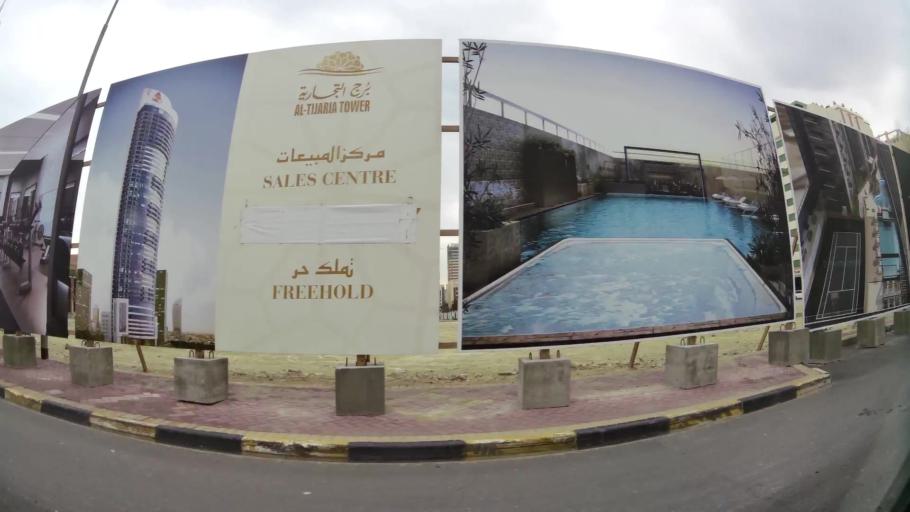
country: BH
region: Muharraq
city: Al Muharraq
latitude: 26.2403
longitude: 50.5933
